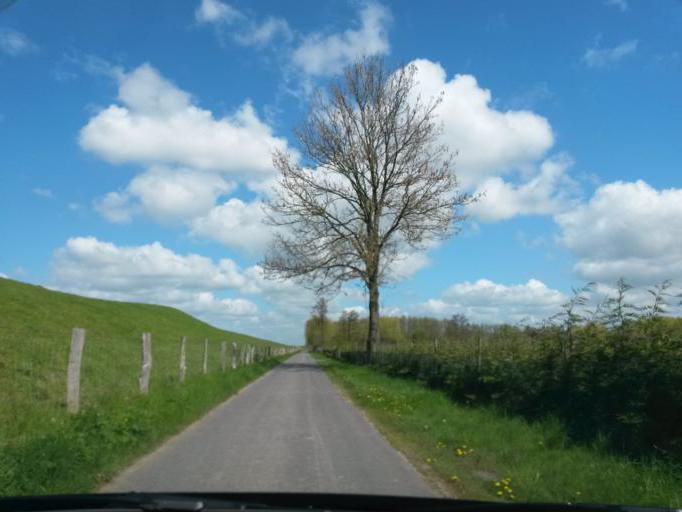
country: DE
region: Schleswig-Holstein
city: Seestermuhe
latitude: 53.6556
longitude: 9.5573
